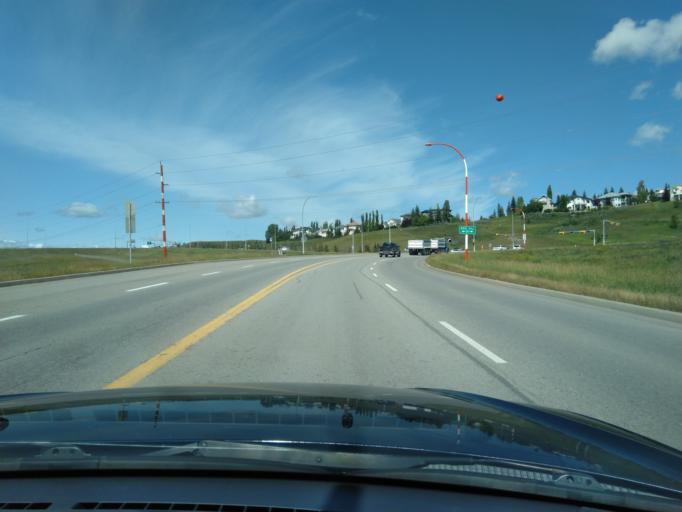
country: CA
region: Alberta
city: Calgary
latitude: 51.1035
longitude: -114.2166
